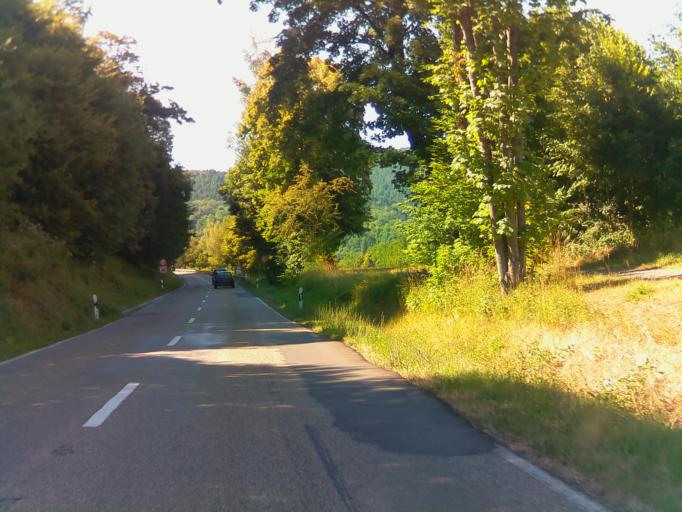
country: DE
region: Bavaria
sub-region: Regierungsbezirk Unterfranken
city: Faulbach
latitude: 49.7811
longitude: 9.4376
